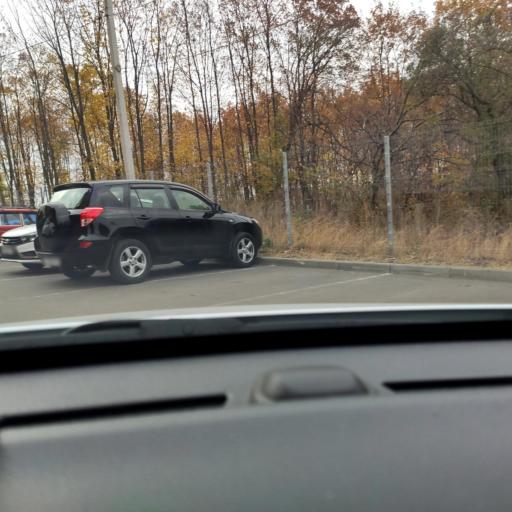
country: RU
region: Voronezj
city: Voronezh
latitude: 51.7038
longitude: 39.2089
